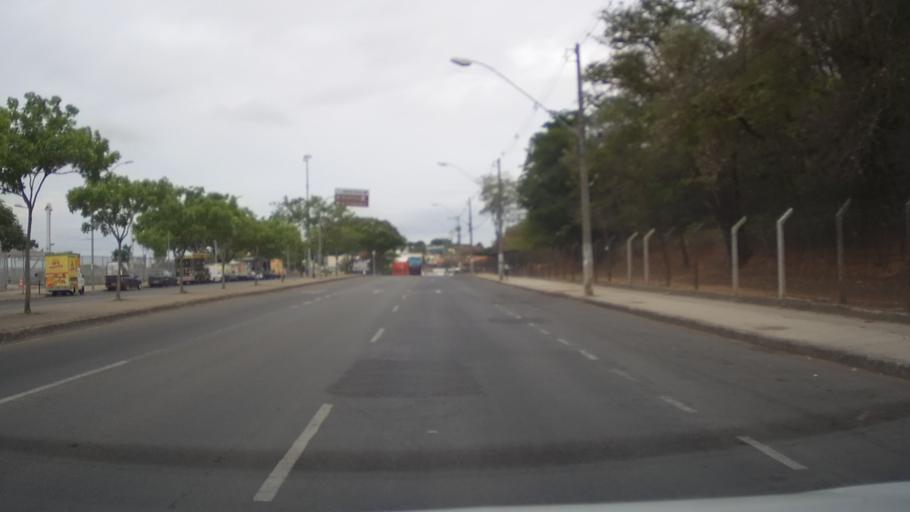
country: BR
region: Minas Gerais
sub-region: Belo Horizonte
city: Belo Horizonte
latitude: -19.8651
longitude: -43.9696
